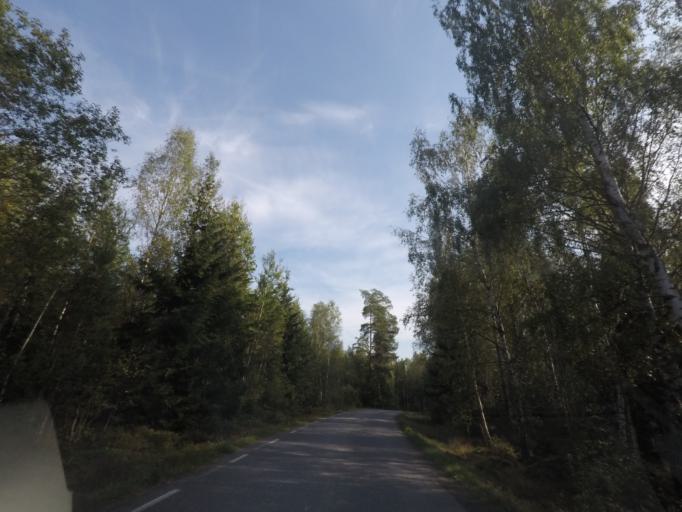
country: SE
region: Vaestmanland
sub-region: Kungsors Kommun
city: Kungsoer
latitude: 59.5101
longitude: 16.1530
